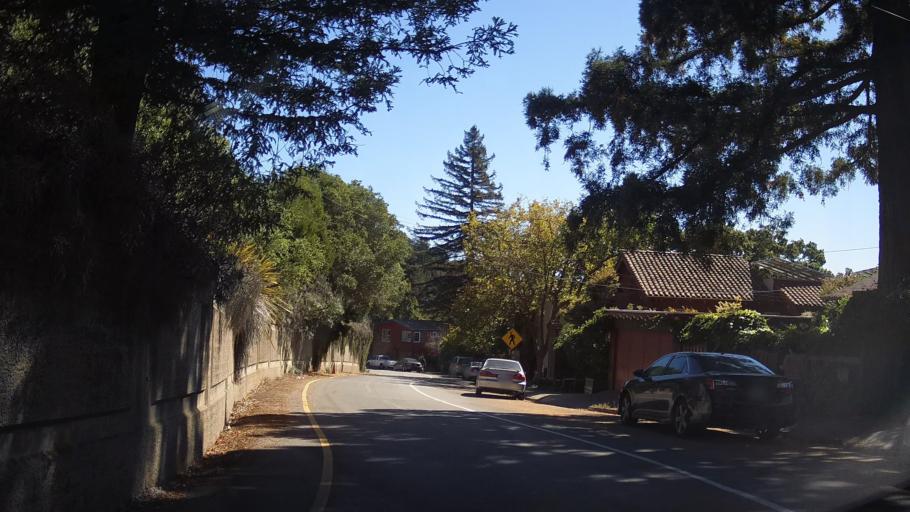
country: US
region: California
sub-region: Alameda County
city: Berkeley
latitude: 37.8892
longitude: -122.2625
